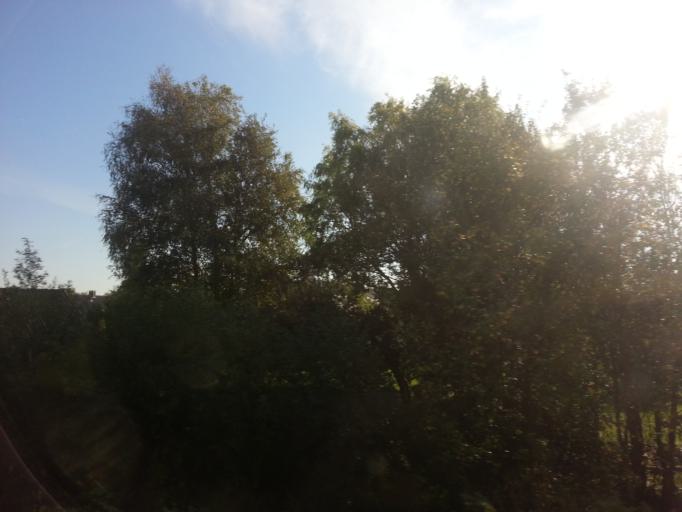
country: NL
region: Gelderland
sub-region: Gemeente Geldermalsen
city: Geldermalsen
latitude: 51.8725
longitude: 5.2727
